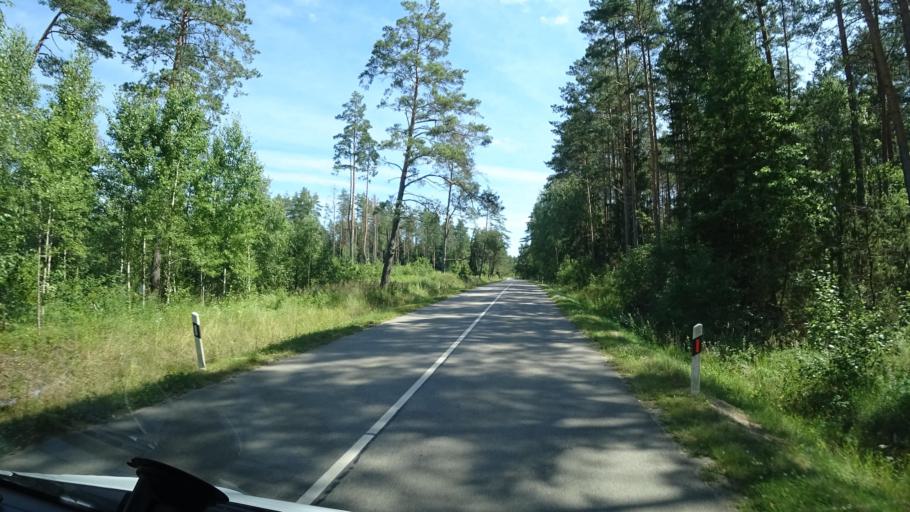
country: LT
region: Vilnius County
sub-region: Trakai
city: Rudiskes
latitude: 54.5103
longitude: 24.9137
